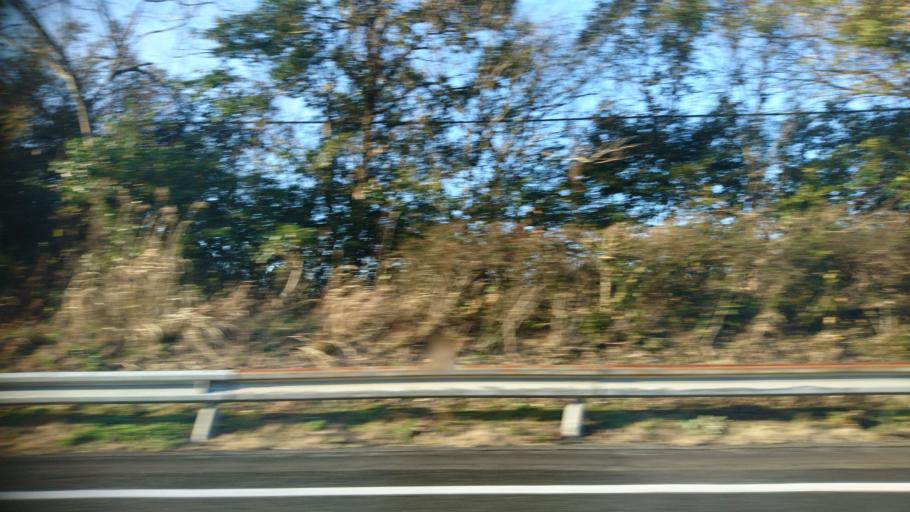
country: JP
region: Miyazaki
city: Miyazaki-shi
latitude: 31.8184
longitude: 131.2725
